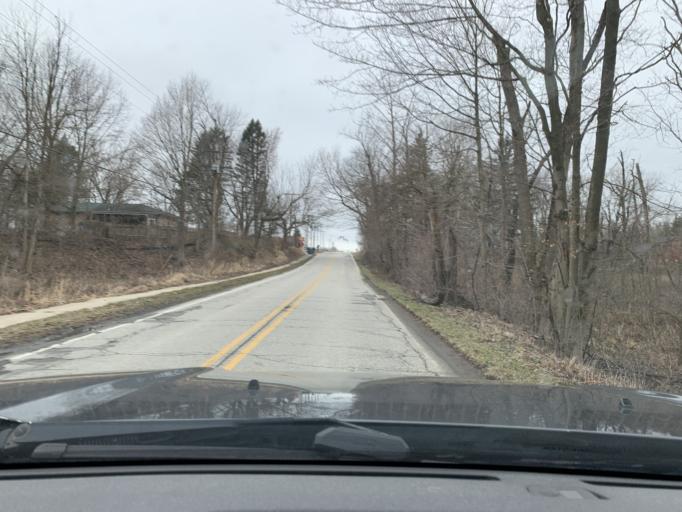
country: US
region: Indiana
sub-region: Porter County
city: Chesterton
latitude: 41.6170
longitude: -87.0323
